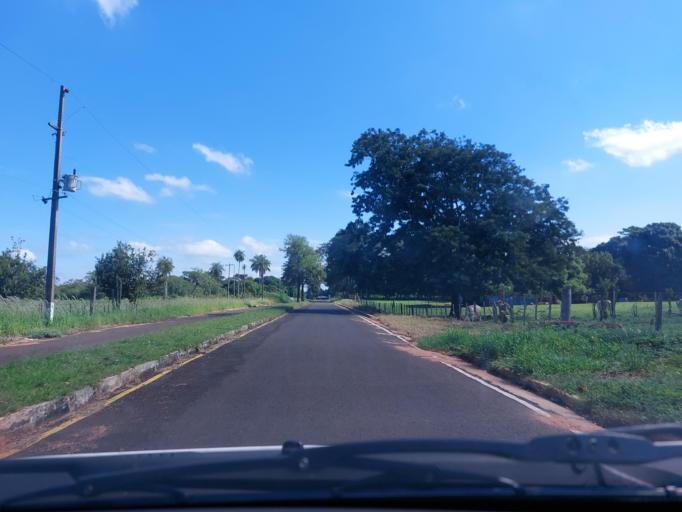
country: PY
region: San Pedro
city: Itacurubi del Rosario
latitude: -24.5313
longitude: -56.5612
